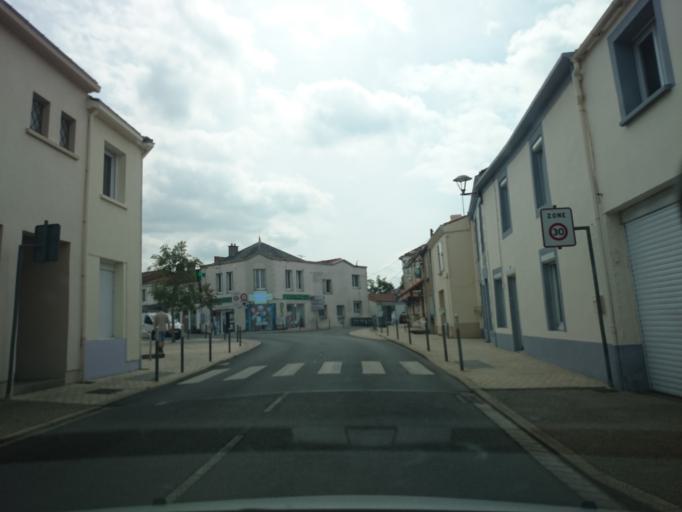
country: FR
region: Pays de la Loire
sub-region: Departement de la Loire-Atlantique
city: La Chevroliere
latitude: 47.0944
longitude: -1.6122
